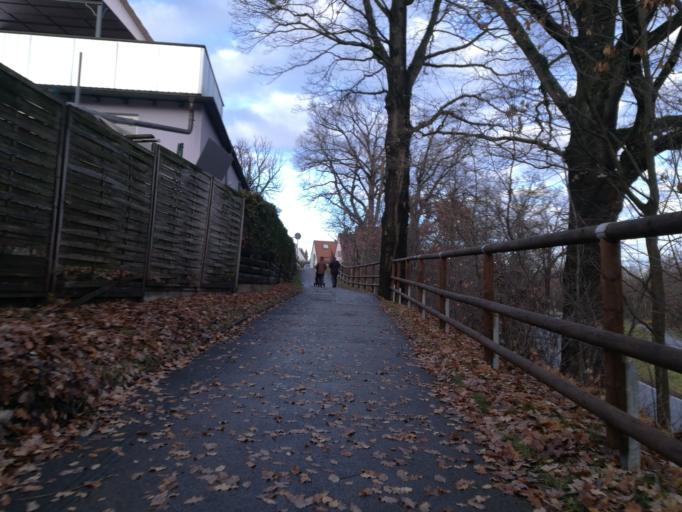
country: DE
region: Bavaria
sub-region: Regierungsbezirk Mittelfranken
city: Furth
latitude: 49.4928
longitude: 10.9639
